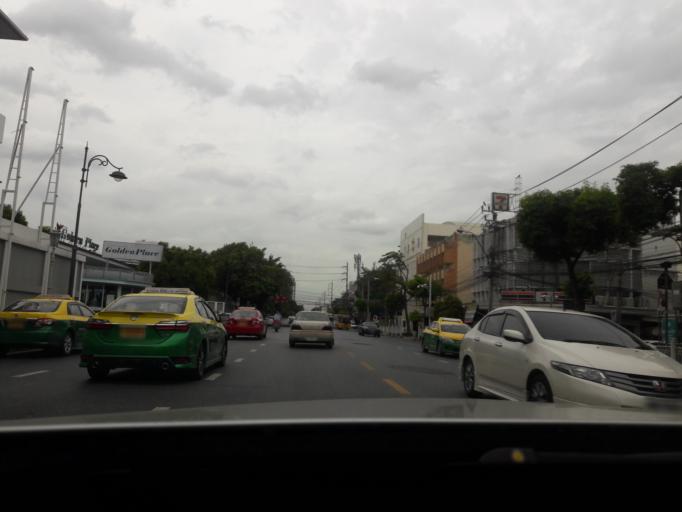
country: TH
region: Bangkok
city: Dusit
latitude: 13.7793
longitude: 100.5142
